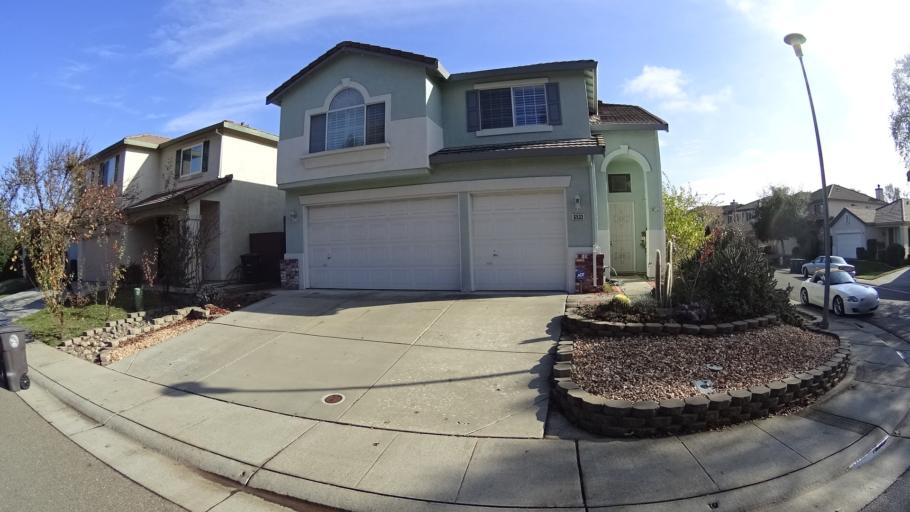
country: US
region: California
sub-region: Sacramento County
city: Antelope
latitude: 38.6906
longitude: -121.3128
